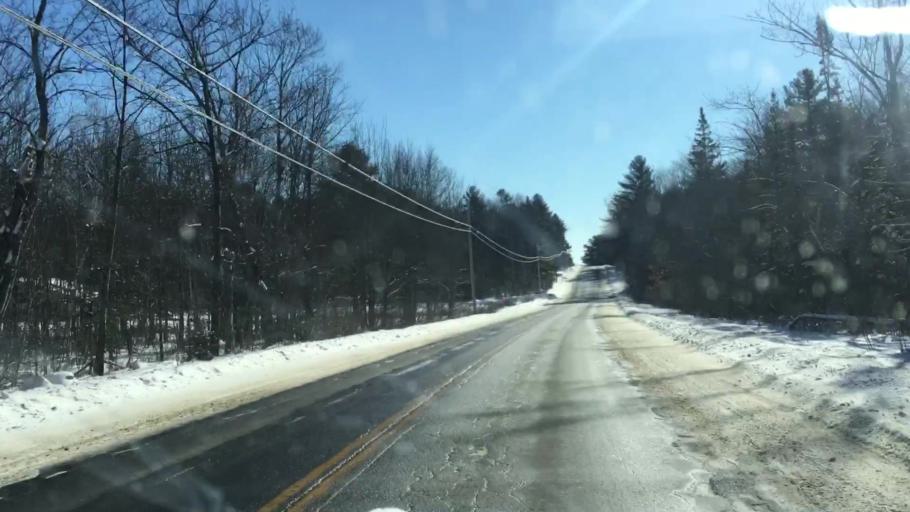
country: US
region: Maine
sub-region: Sagadahoc County
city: Topsham
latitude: 43.9235
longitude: -70.0433
